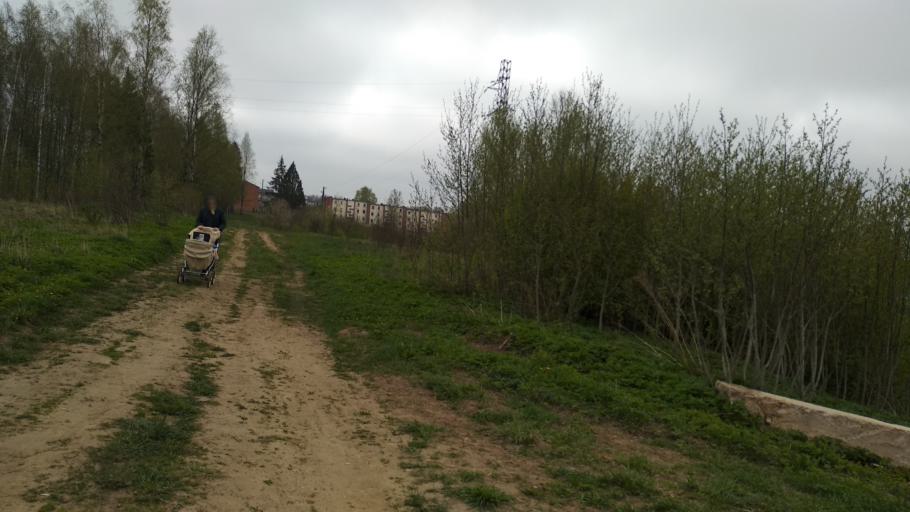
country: LV
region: Malpils
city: Malpils
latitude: 57.0154
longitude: 24.9523
